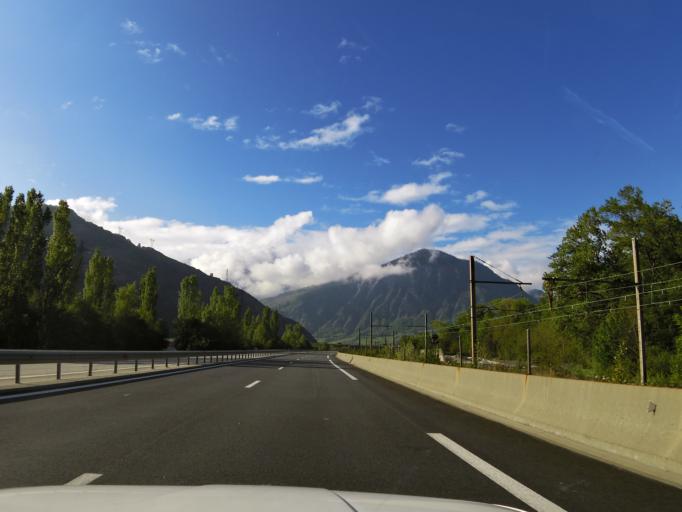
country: FR
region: Rhone-Alpes
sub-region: Departement de la Savoie
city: Saint-Jean-de-Maurienne
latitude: 45.2936
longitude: 6.3562
